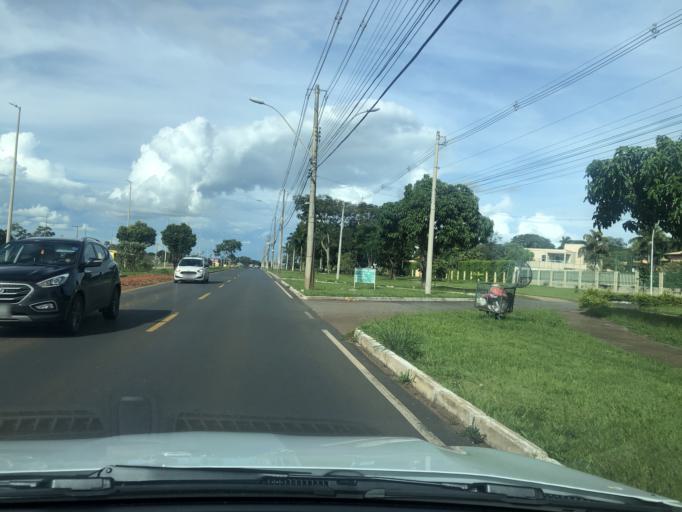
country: BR
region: Federal District
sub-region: Brasilia
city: Brasilia
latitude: -15.8742
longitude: -47.9545
